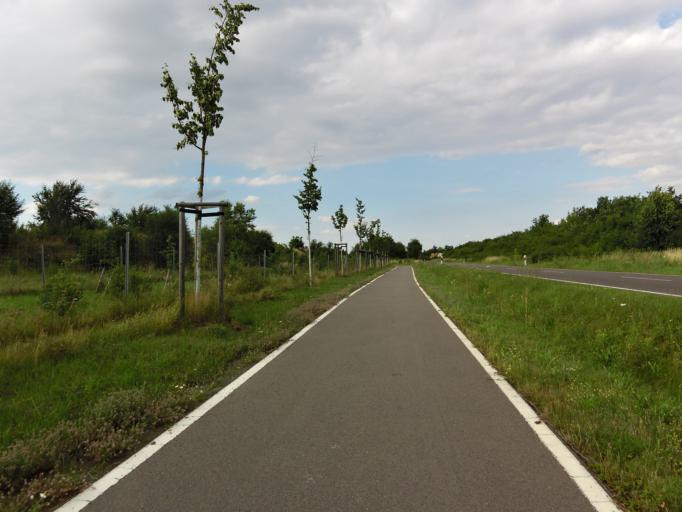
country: DE
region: Saxony
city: Zwenkau
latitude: 51.2646
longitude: 12.2940
